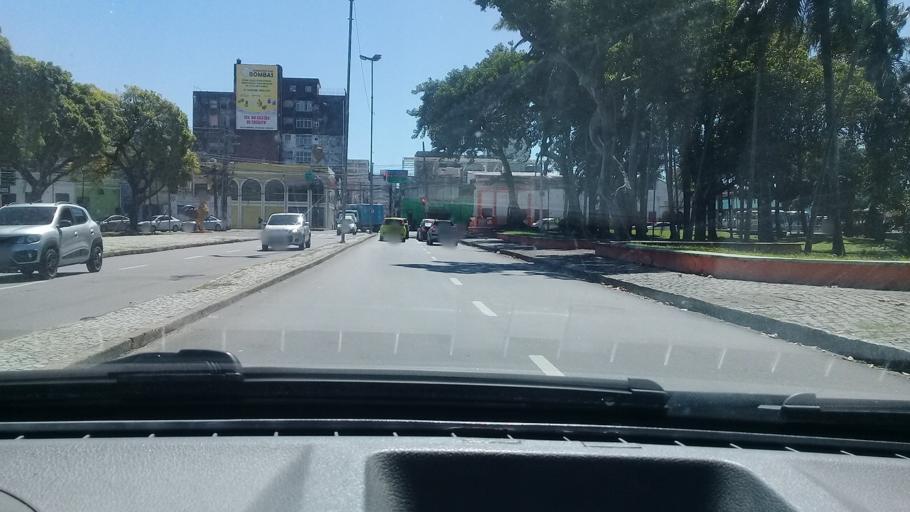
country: BR
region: Pernambuco
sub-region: Recife
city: Recife
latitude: -8.0727
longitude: -34.8851
